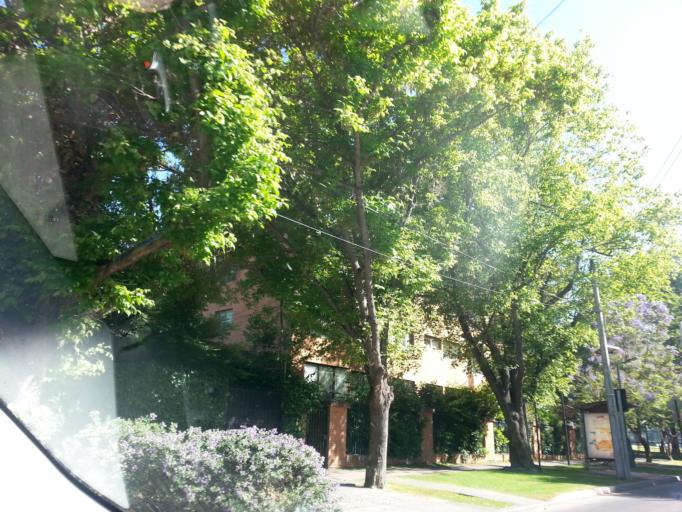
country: CL
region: Santiago Metropolitan
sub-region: Provincia de Santiago
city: Villa Presidente Frei, Nunoa, Santiago, Chile
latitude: -33.3890
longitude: -70.5896
